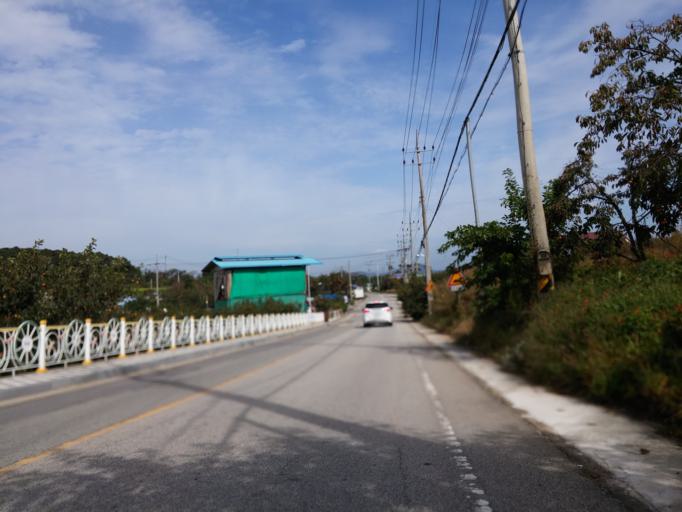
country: KR
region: Chungcheongnam-do
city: Yonmu
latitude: 36.1693
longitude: 127.1104
